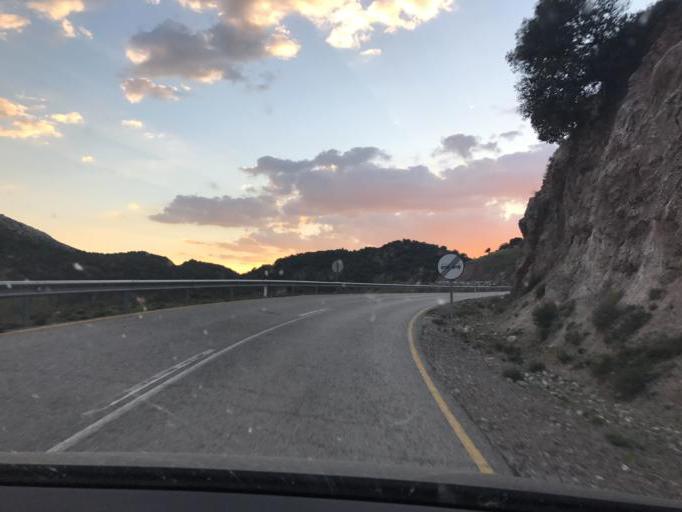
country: ES
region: Andalusia
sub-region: Provincia de Granada
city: Diezma
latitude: 37.3046
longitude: -3.4296
